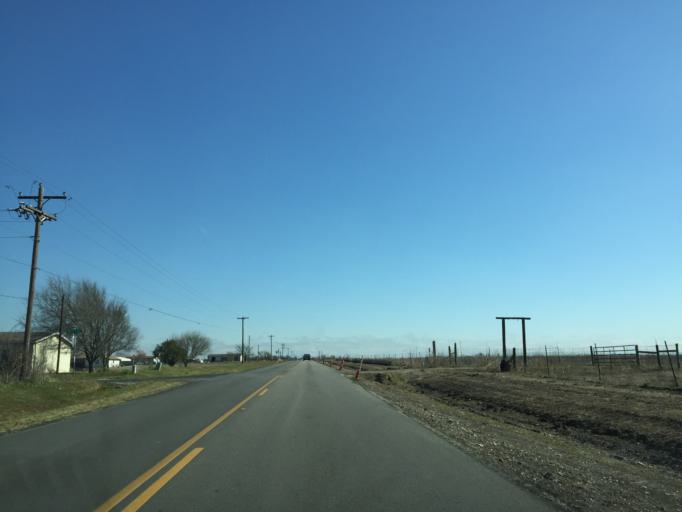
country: US
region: Texas
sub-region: Williamson County
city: Serenada
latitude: 30.7276
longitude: -97.6299
